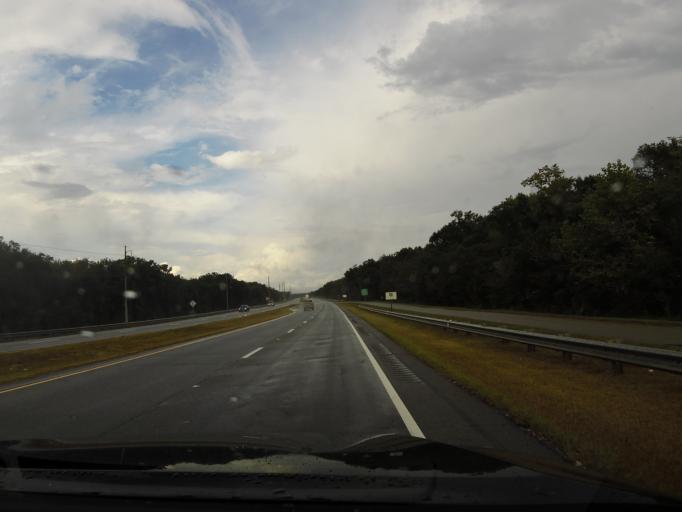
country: US
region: Georgia
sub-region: Wayne County
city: Jesup
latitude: 31.6687
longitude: -81.8342
